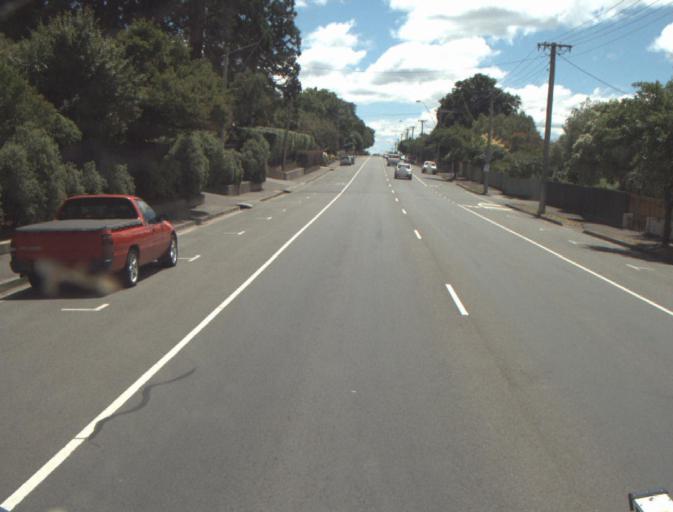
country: AU
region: Tasmania
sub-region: Launceston
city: East Launceston
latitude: -41.4404
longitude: 147.1601
